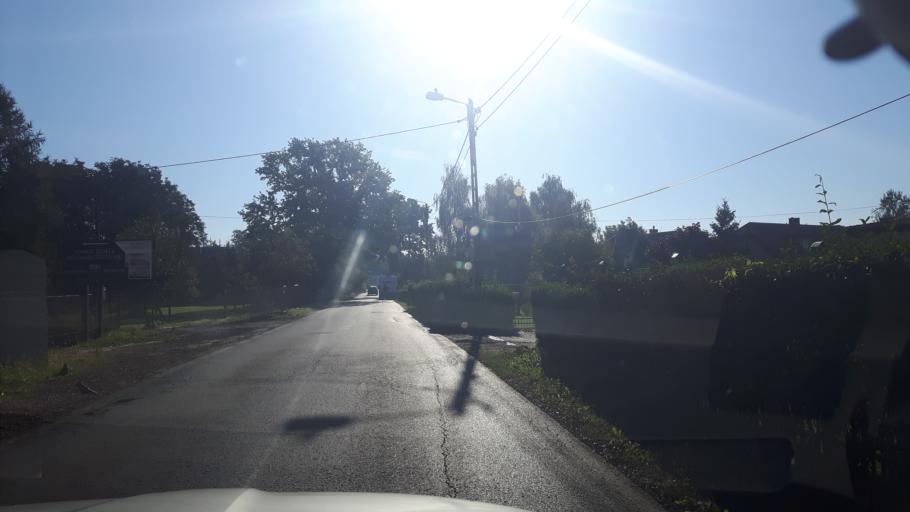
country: PL
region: Masovian Voivodeship
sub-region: Powiat legionowski
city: Stanislawow Pierwszy
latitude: 52.3506
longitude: 21.0249
